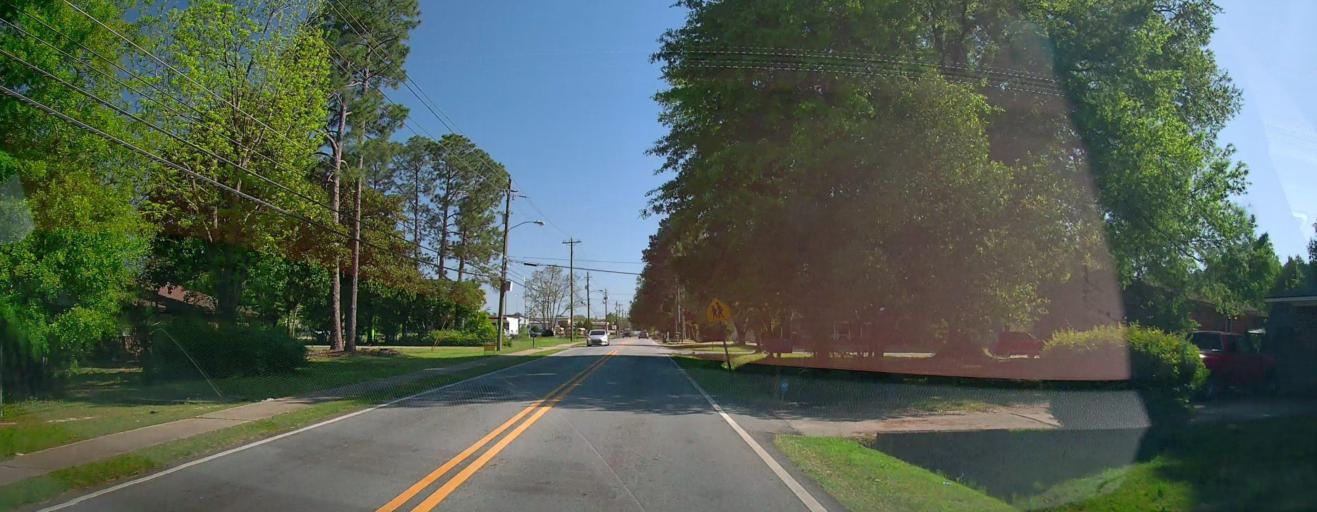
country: US
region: Georgia
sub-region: Houston County
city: Warner Robins
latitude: 32.6335
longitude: -83.6320
